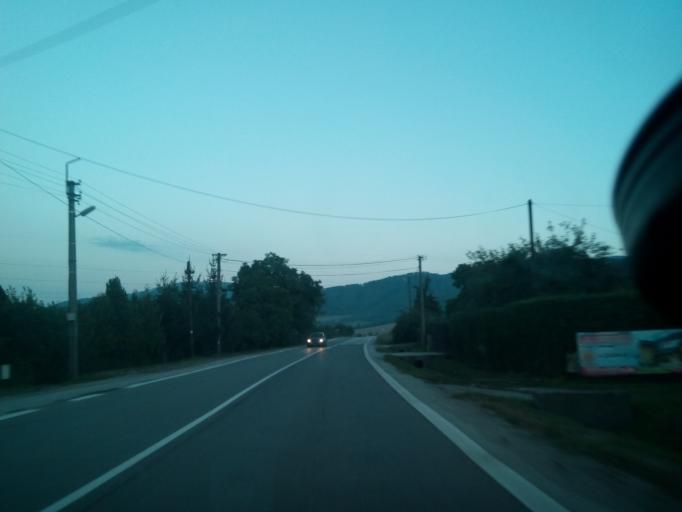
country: SK
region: Kosicky
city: Dobsina
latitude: 48.7230
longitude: 20.4176
